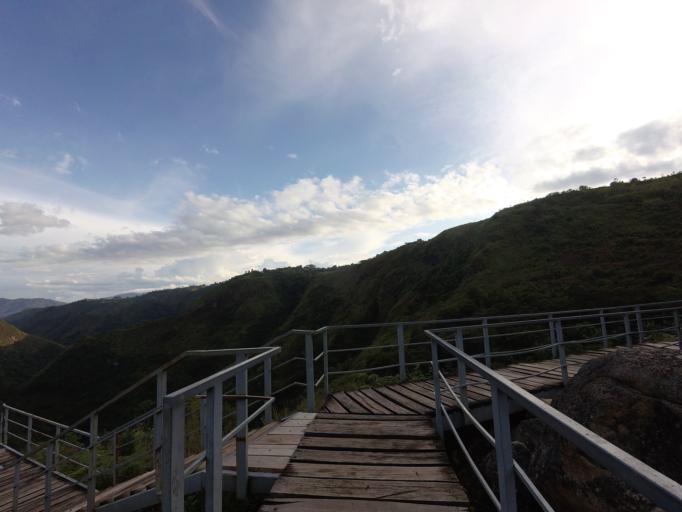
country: CO
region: Huila
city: San Agustin
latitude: 1.9031
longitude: -76.2674
